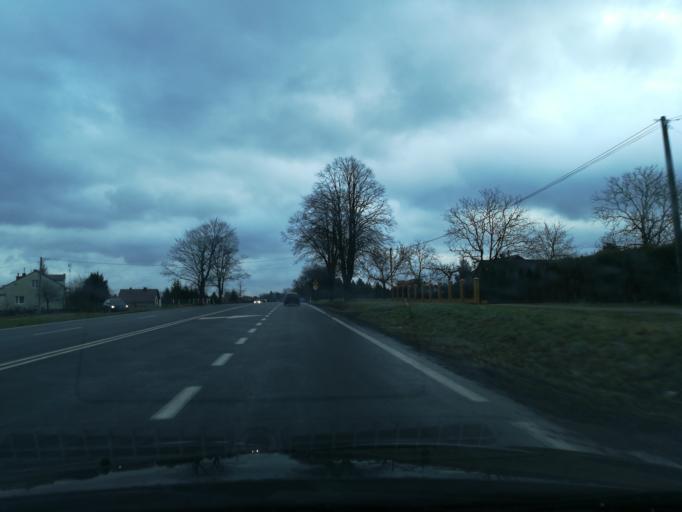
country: PL
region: Subcarpathian Voivodeship
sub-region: Powiat lancucki
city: Kosina
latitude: 50.0733
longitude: 22.3174
